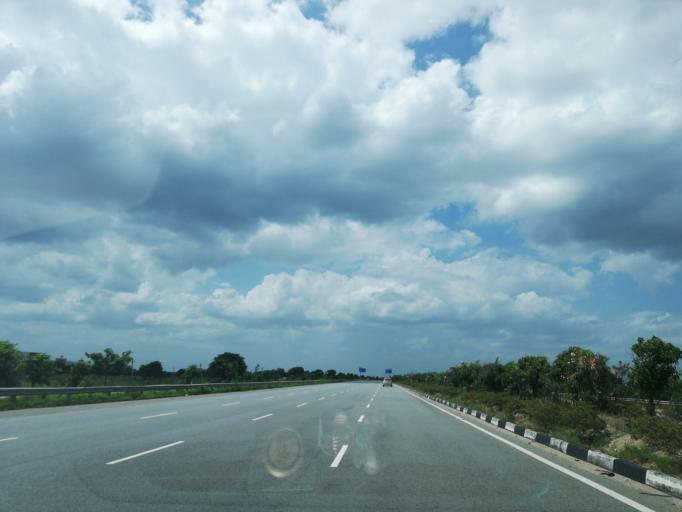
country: IN
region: Telangana
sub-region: Medak
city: Serilingampalle
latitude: 17.4517
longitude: 78.2537
